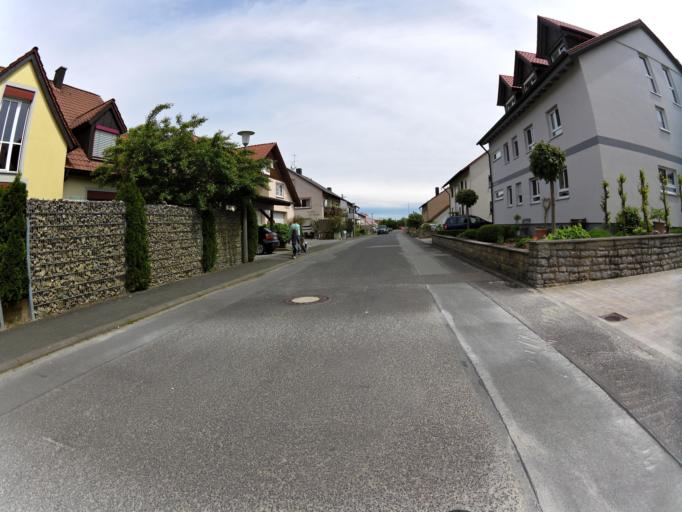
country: DE
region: Bavaria
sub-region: Regierungsbezirk Unterfranken
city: Nordheim
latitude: 49.8581
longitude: 10.1876
